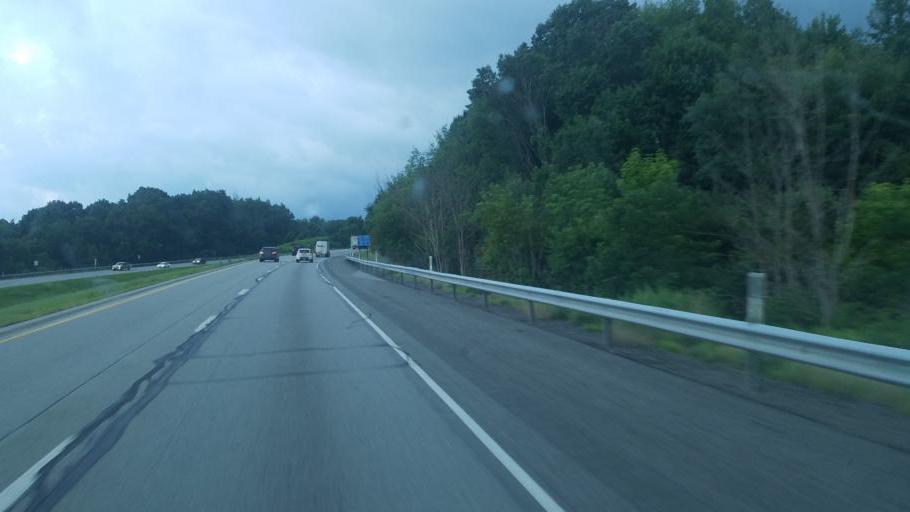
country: US
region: Pennsylvania
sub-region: Butler County
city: Slippery Rock
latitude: 40.9971
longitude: -80.1207
